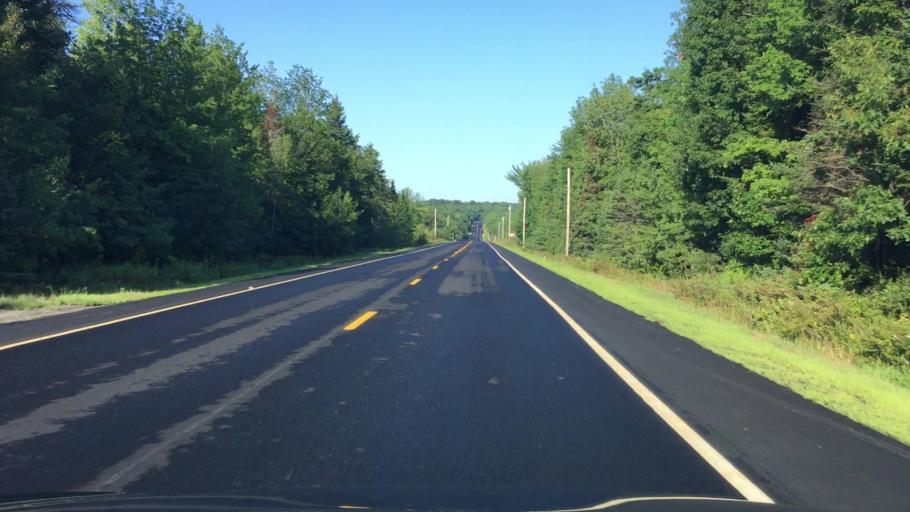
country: US
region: Maine
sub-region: Waldo County
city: Searsmont
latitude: 44.4050
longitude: -69.2281
